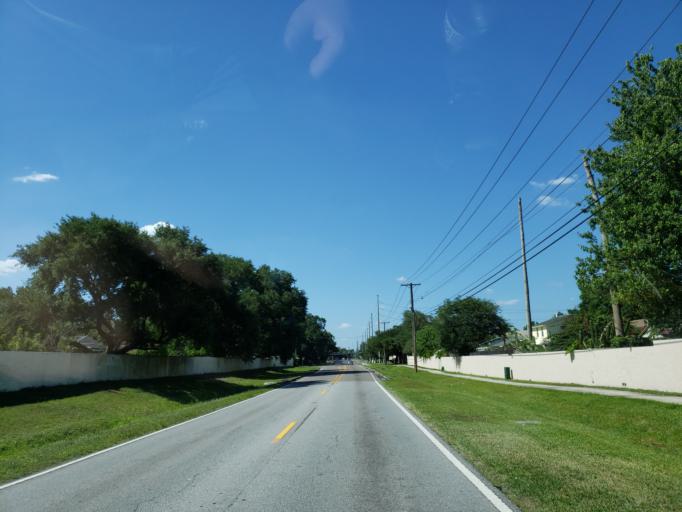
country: US
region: Florida
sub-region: Hillsborough County
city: Mango
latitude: 27.9725
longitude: -82.3105
